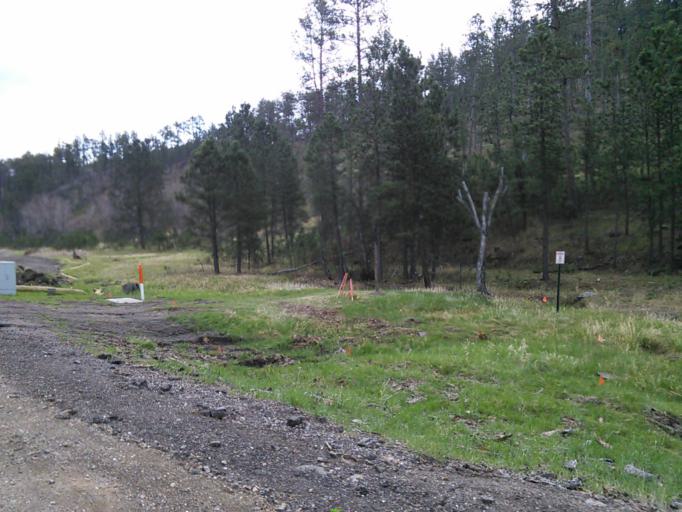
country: US
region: South Dakota
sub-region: Custer County
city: Custer
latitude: 43.7606
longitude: -103.4796
